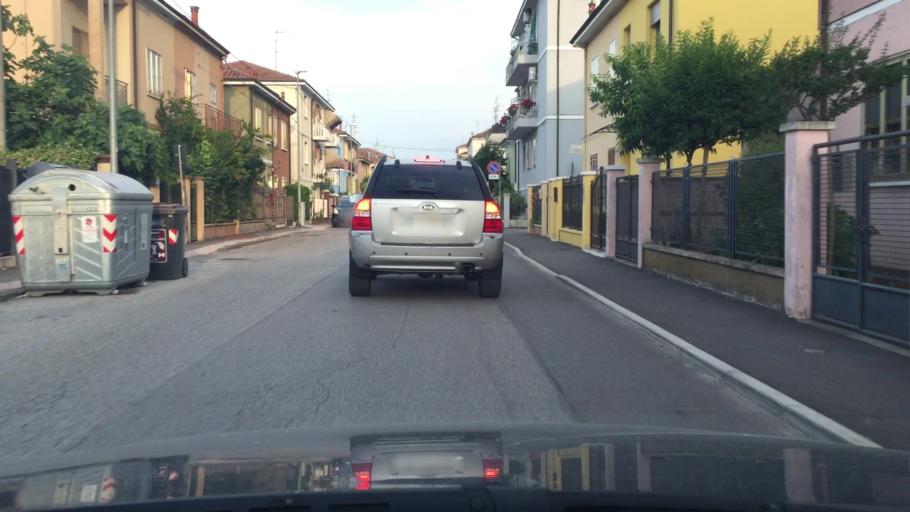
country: IT
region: Emilia-Romagna
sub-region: Provincia di Ferrara
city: Ferrara
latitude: 44.8221
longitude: 11.6106
